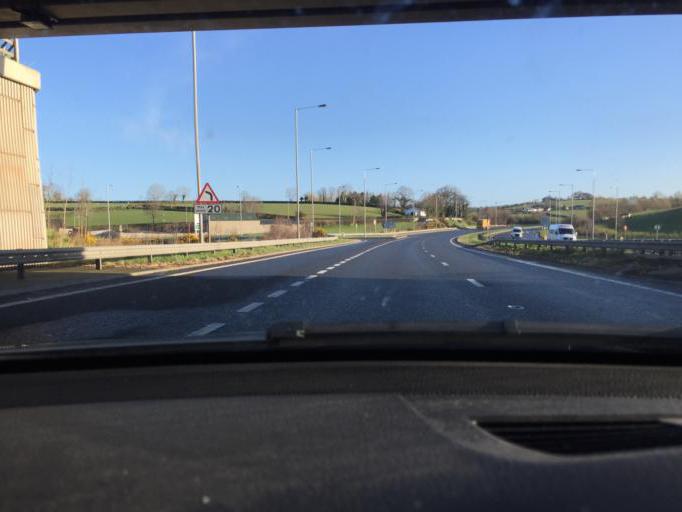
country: GB
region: Northern Ireland
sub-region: Banbridge District
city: Banbridge
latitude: 54.3544
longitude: -6.2403
